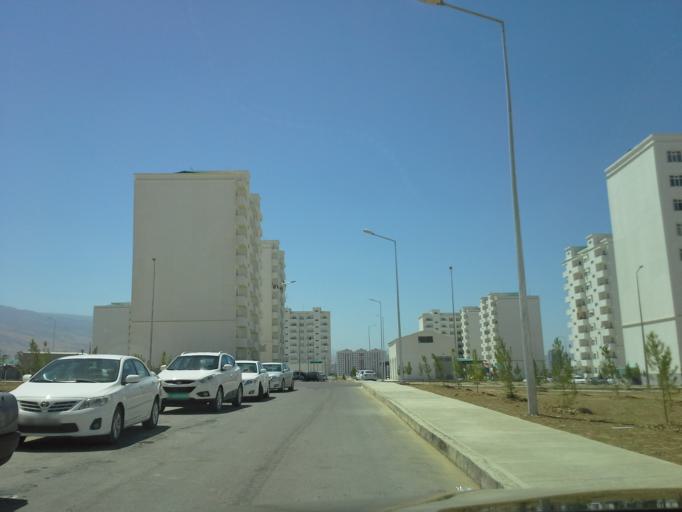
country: TM
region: Ahal
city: Ashgabat
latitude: 37.8889
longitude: 58.4102
